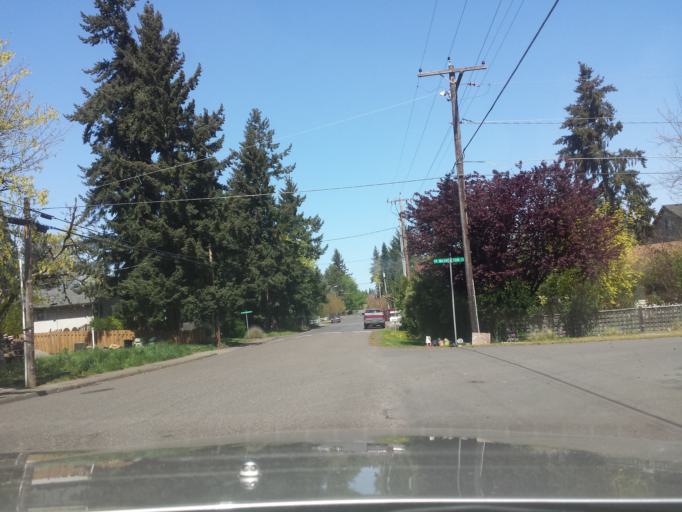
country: US
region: Oregon
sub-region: Washington County
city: Aloha
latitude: 45.4838
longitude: -122.8576
